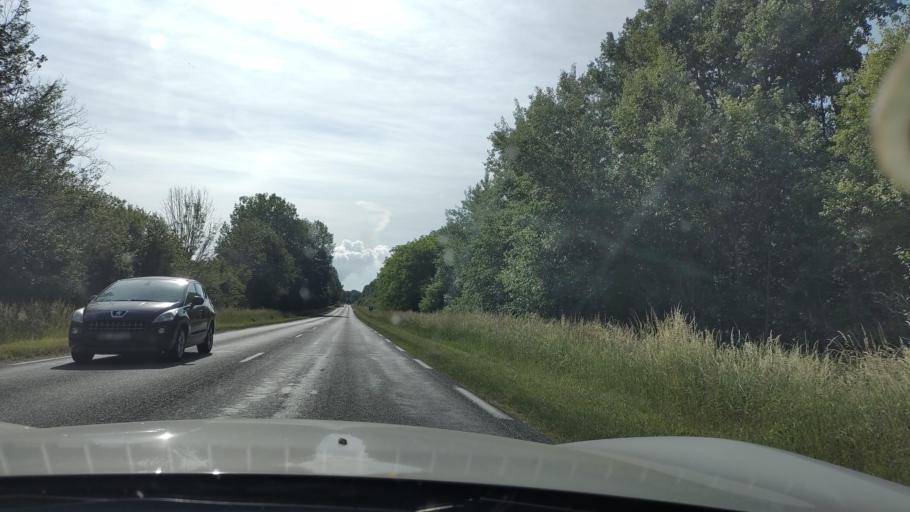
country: FR
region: Ile-de-France
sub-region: Departement de Seine-et-Marne
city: Sourdun
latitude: 48.5309
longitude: 3.3888
